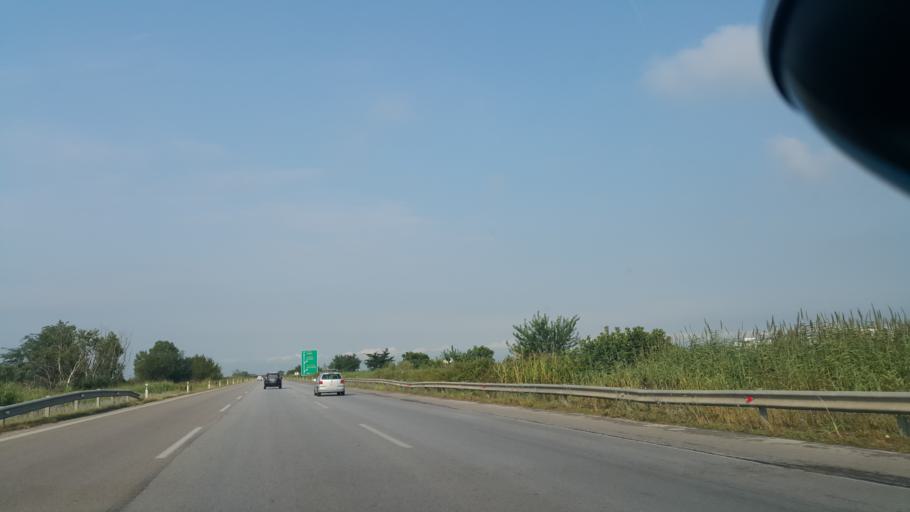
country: GR
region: Central Macedonia
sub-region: Nomos Thessalonikis
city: Chalastra
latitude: 40.6204
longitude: 22.7550
